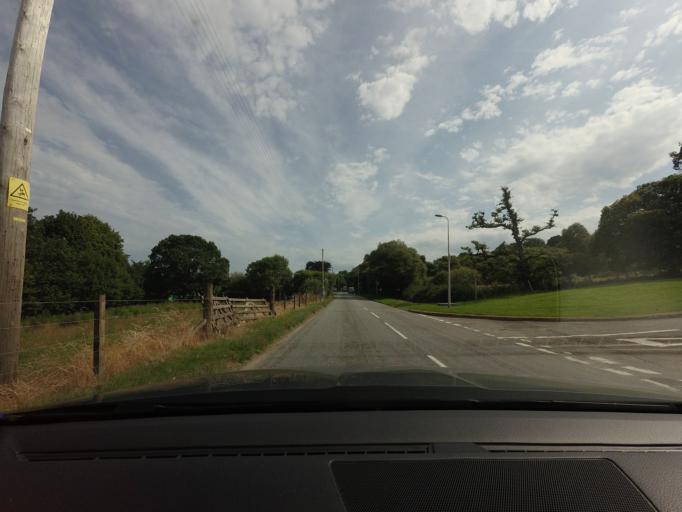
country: GB
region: Scotland
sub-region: Highland
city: Alness
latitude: 57.8796
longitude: -4.3612
